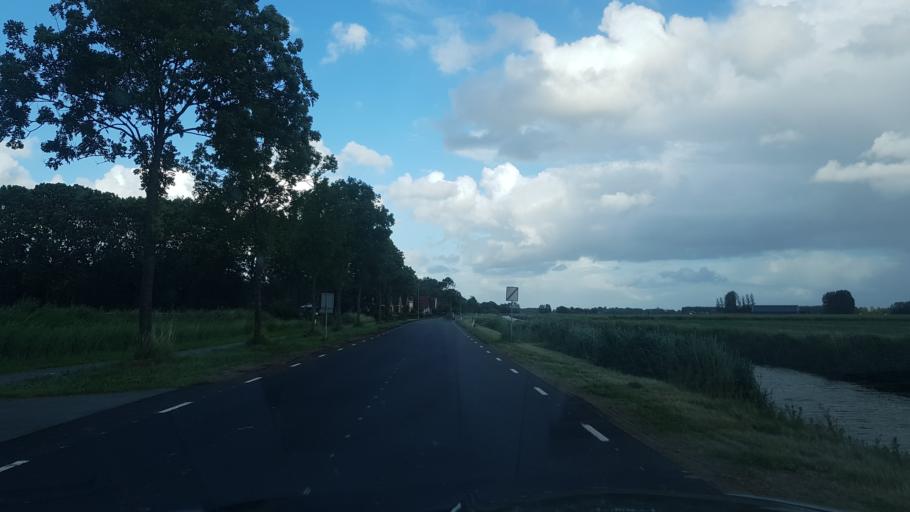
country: NL
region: Groningen
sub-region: Gemeente Appingedam
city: Appingedam
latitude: 53.3267
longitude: 6.7508
